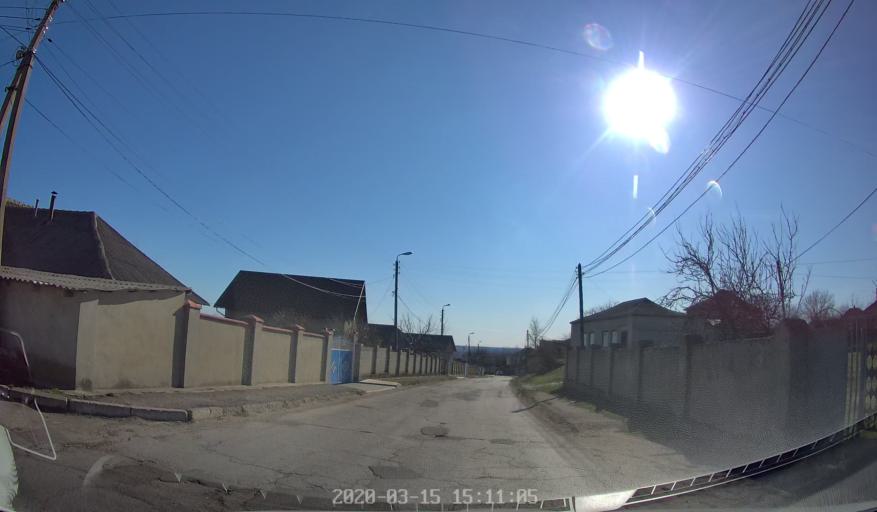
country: MD
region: Orhei
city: Orhei
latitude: 47.2644
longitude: 28.7786
